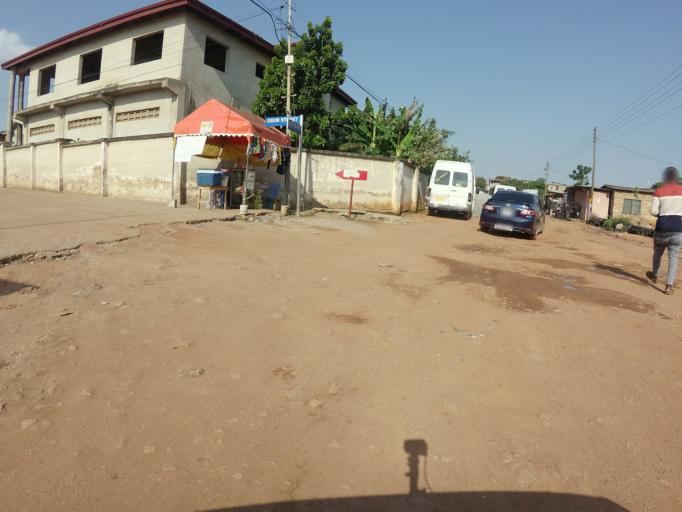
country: GH
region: Greater Accra
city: Dome
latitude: 5.6092
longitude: -0.2438
